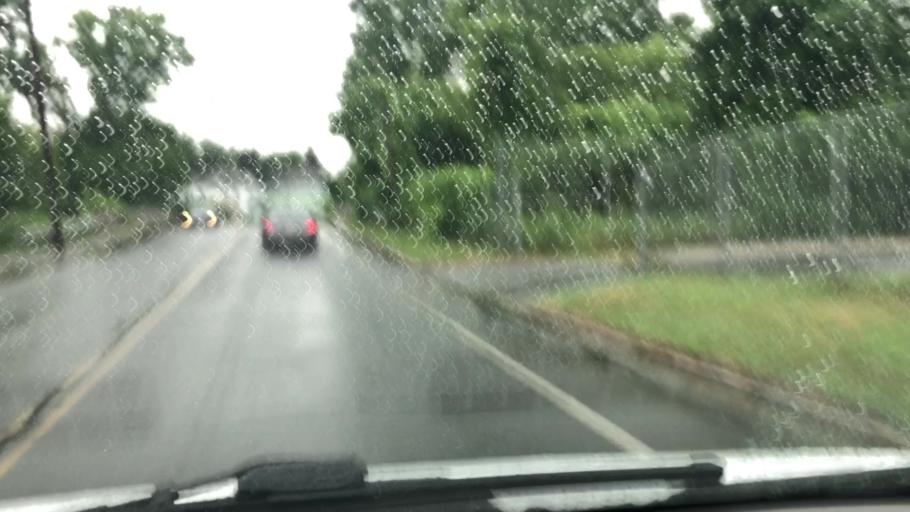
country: US
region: Massachusetts
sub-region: Berkshire County
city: Pittsfield
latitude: 42.4517
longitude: -73.2269
